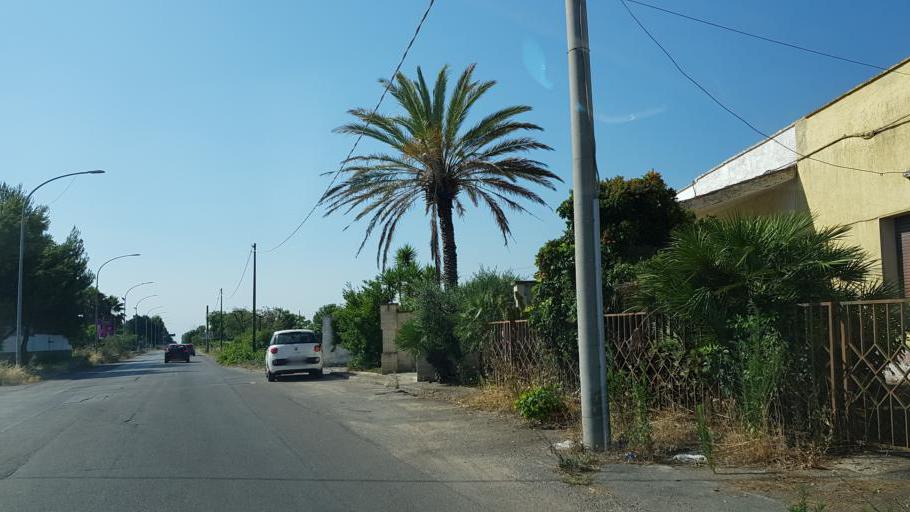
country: IT
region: Apulia
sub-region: Provincia di Brindisi
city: San Donaci
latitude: 40.4414
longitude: 17.9292
